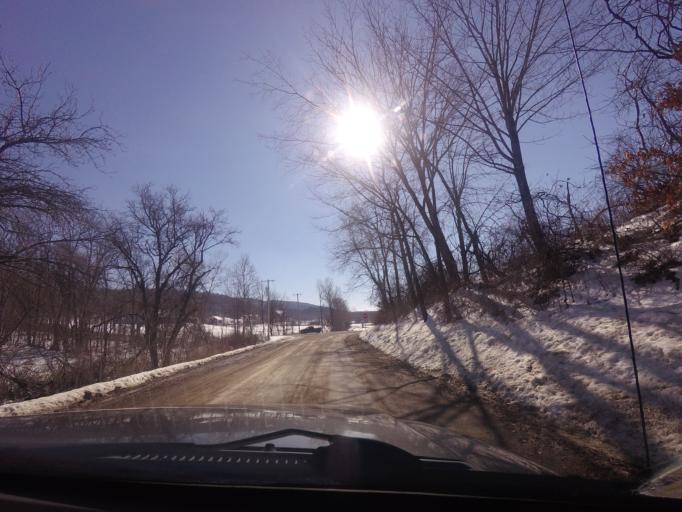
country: US
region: New York
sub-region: Washington County
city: Cambridge
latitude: 43.1090
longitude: -73.4070
